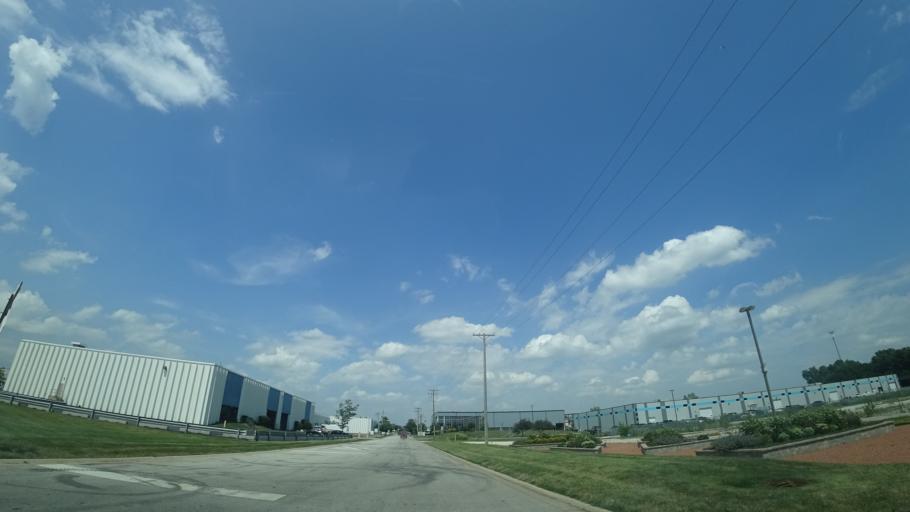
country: US
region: Illinois
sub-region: Cook County
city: Crestwood
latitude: 41.6759
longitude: -87.7684
